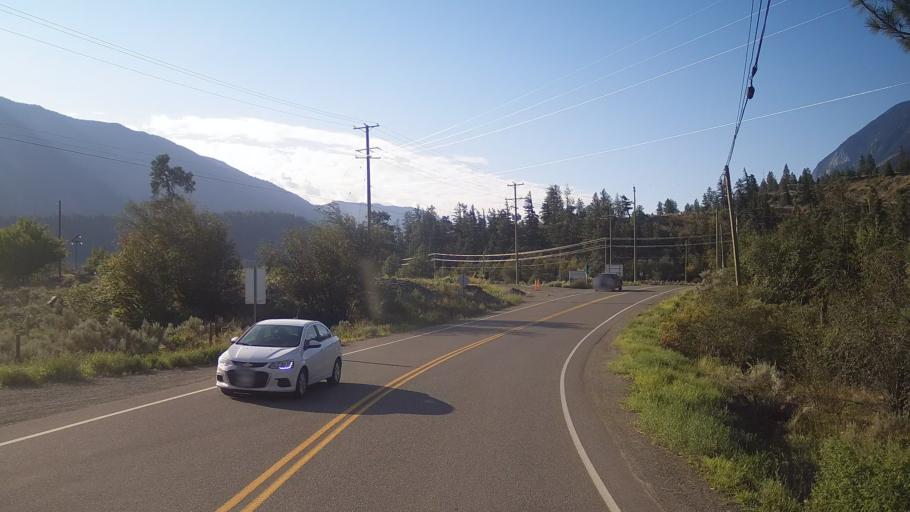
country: CA
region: British Columbia
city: Lillooet
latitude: 50.6786
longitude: -121.9324
